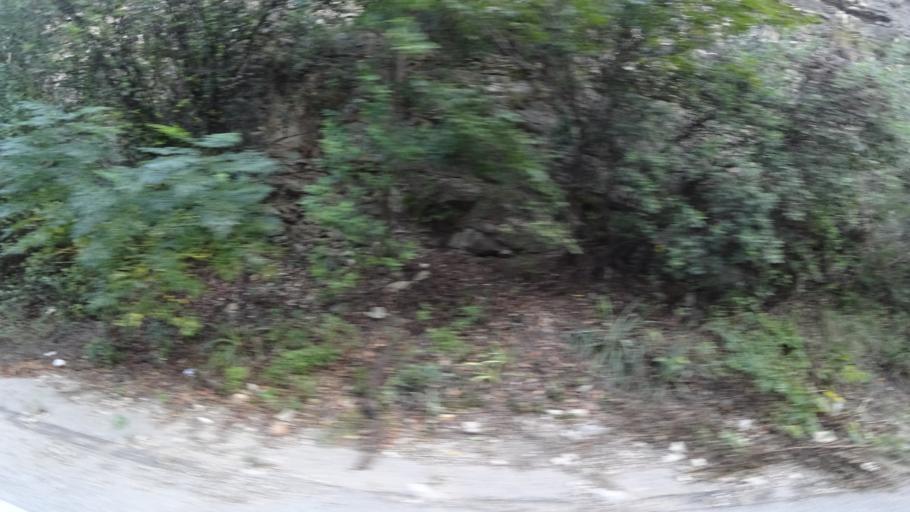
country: US
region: Texas
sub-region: Travis County
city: Rollingwood
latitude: 30.2908
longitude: -97.7893
